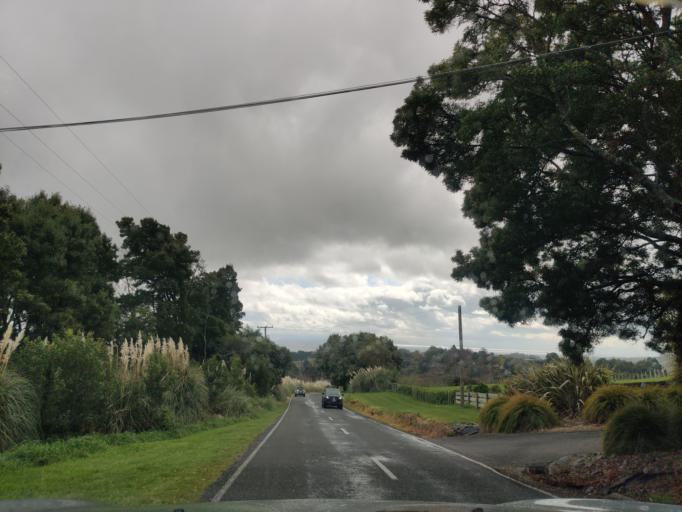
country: NZ
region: Hawke's Bay
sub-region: Hastings District
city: Hastings
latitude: -39.6917
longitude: 176.9004
